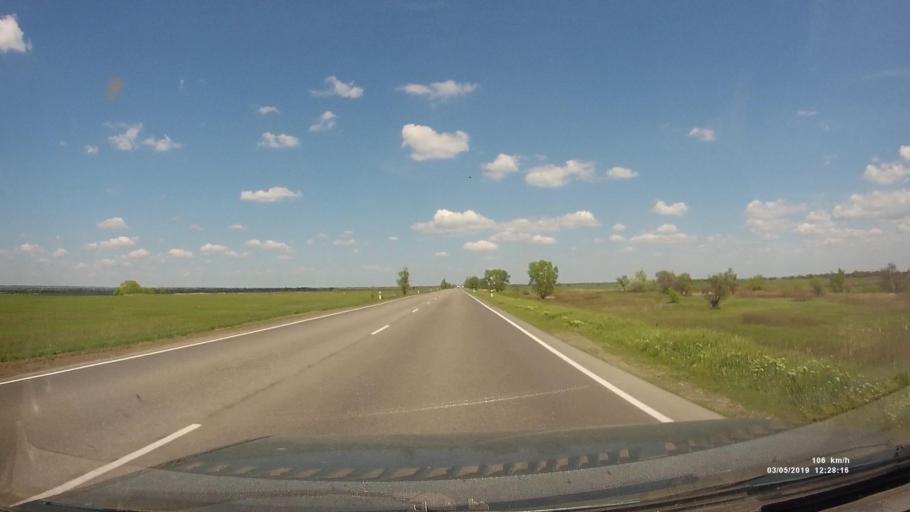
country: RU
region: Rostov
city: Semikarakorsk
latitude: 47.4706
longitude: 40.7273
